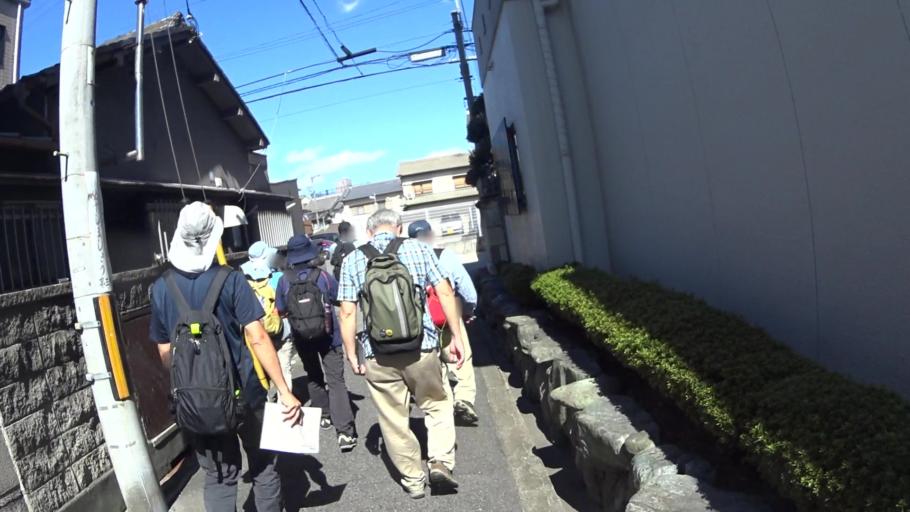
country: JP
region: Osaka
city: Yao
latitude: 34.6321
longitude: 135.5576
